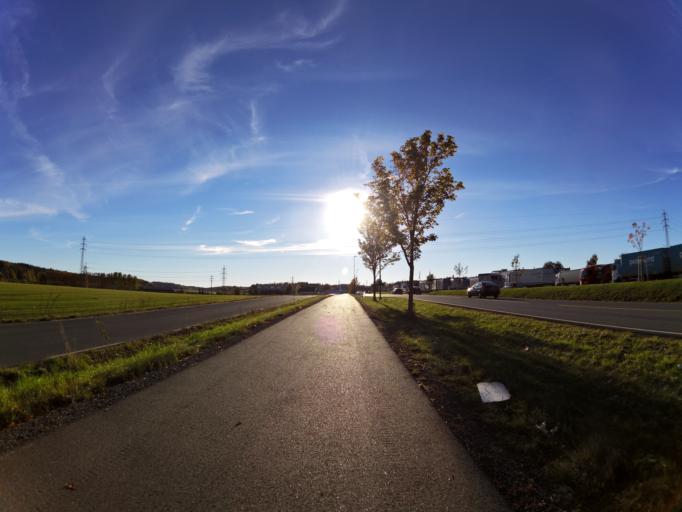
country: NO
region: Ostfold
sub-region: Sarpsborg
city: Sarpsborg
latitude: 59.2643
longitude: 11.1191
